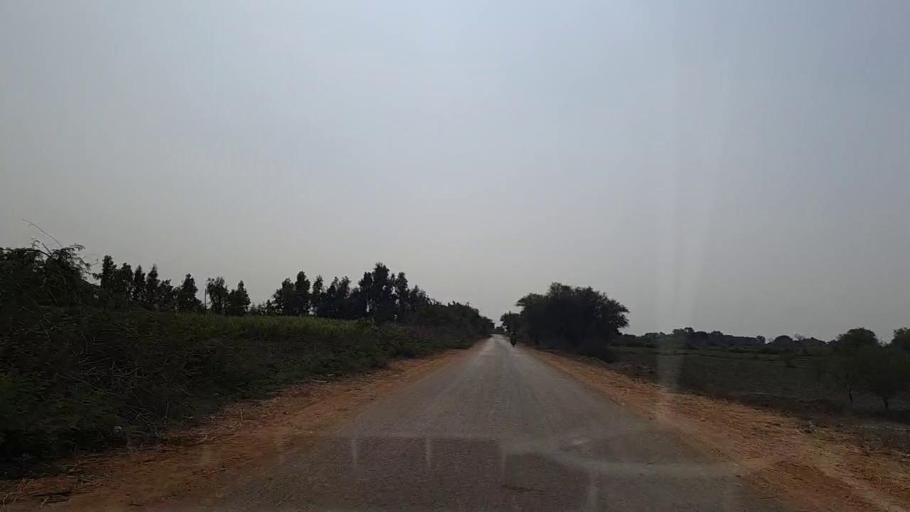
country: PK
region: Sindh
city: Chuhar Jamali
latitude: 24.2512
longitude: 67.9058
